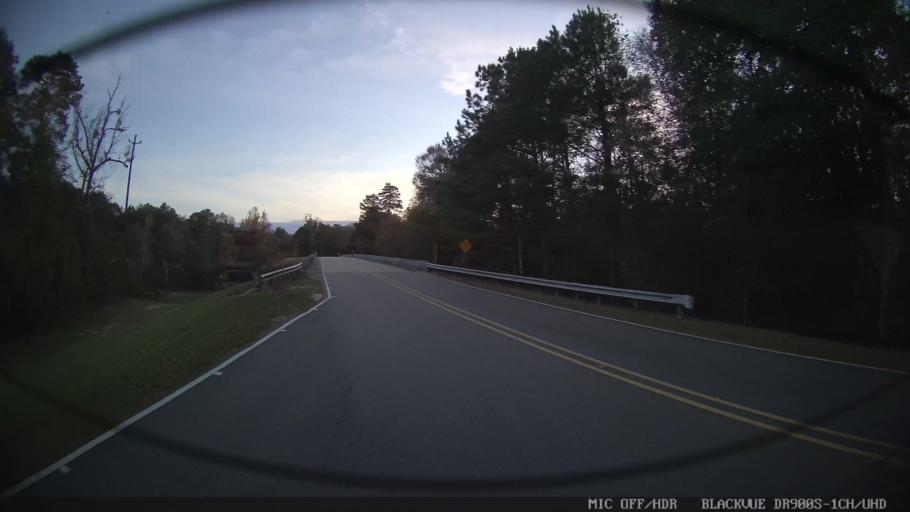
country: US
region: Mississippi
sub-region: Stone County
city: Wiggins
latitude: 31.0544
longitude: -89.1911
